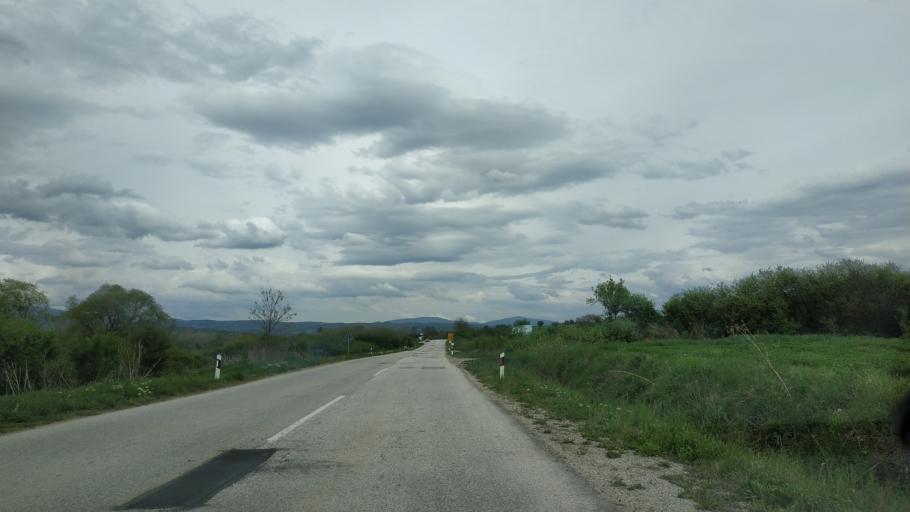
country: RS
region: Central Serbia
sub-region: Zajecarski Okrug
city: Soko Banja
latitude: 43.6536
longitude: 21.7694
